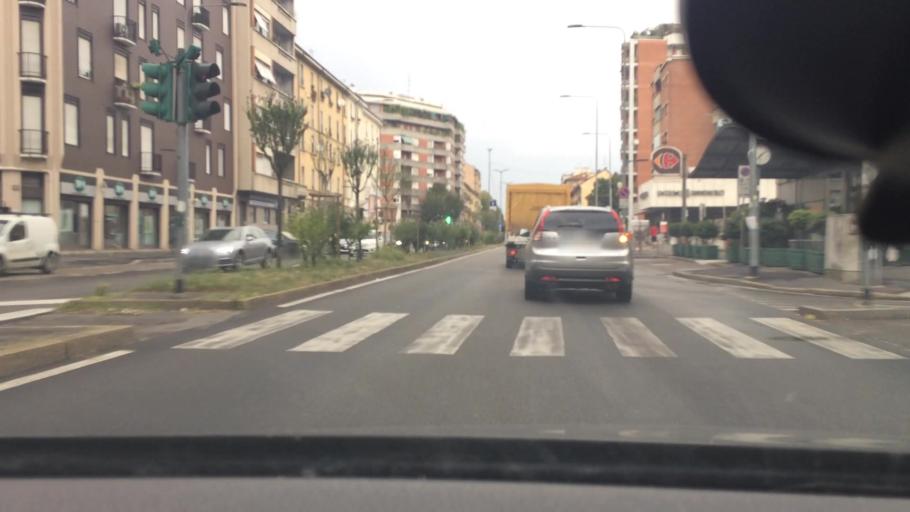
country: IT
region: Lombardy
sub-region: Citta metropolitana di Milano
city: Sesto San Giovanni
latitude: 45.5022
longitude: 9.2216
